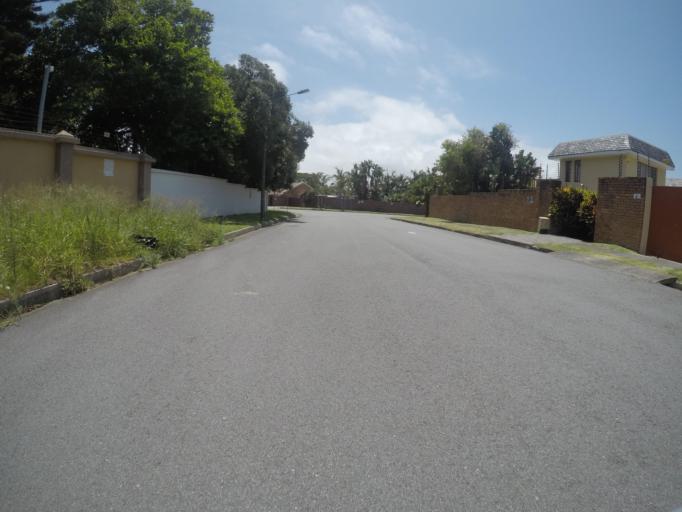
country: ZA
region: Eastern Cape
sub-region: Buffalo City Metropolitan Municipality
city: East London
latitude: -32.9971
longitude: 27.9281
